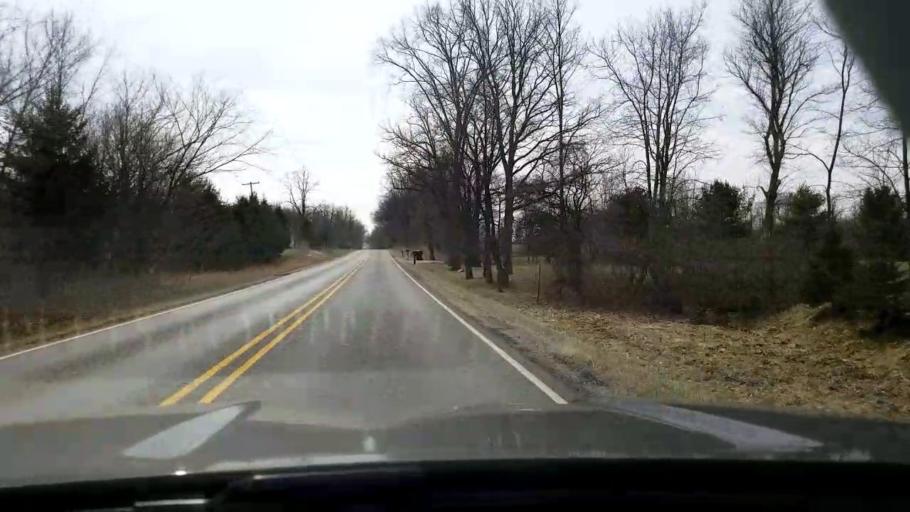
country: US
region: Michigan
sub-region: Jackson County
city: Spring Arbor
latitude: 42.0770
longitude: -84.5168
